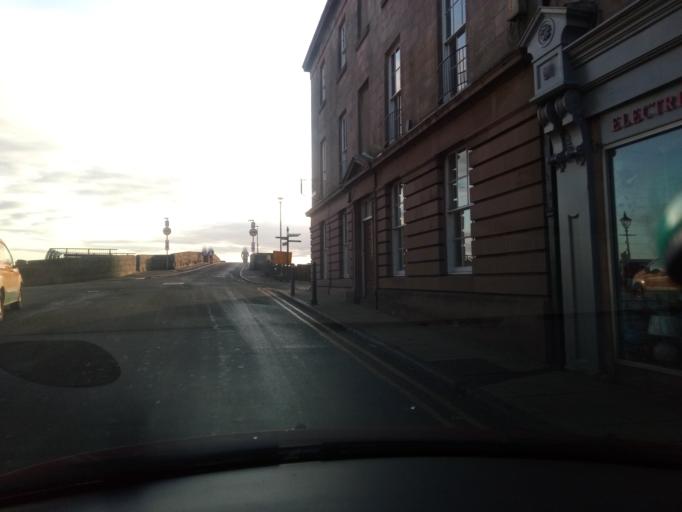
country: GB
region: England
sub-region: Northumberland
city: Berwick-Upon-Tweed
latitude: 55.7686
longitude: -2.0055
